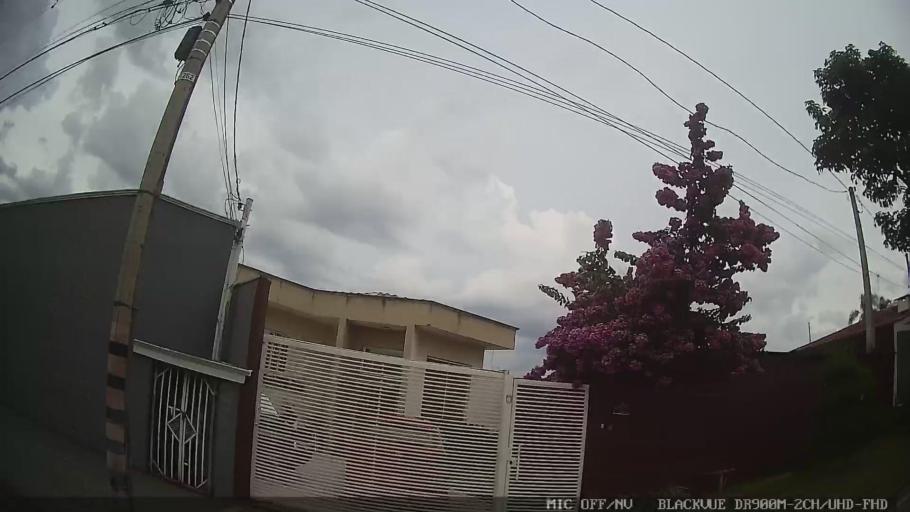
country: BR
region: Sao Paulo
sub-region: Atibaia
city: Atibaia
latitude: -23.1344
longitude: -46.5611
